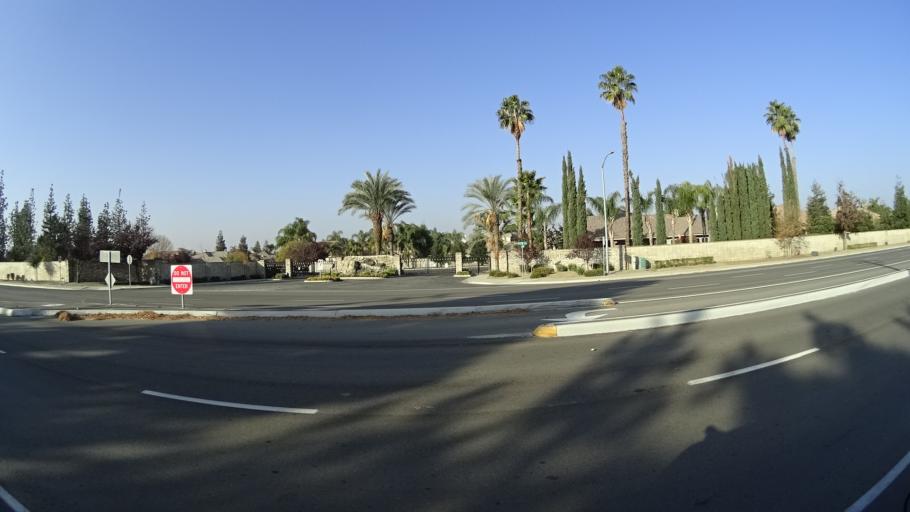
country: US
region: California
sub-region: Kern County
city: Rosedale
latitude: 35.3735
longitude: -119.1454
